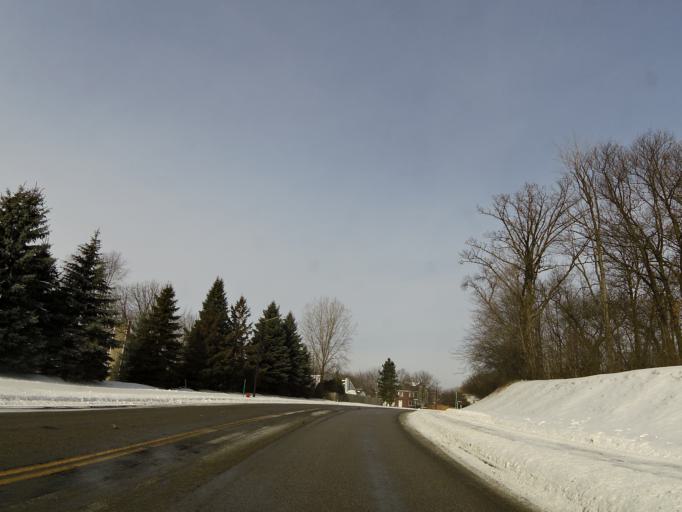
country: US
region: Minnesota
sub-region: Carver County
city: Chanhassen
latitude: 44.8864
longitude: -93.5168
